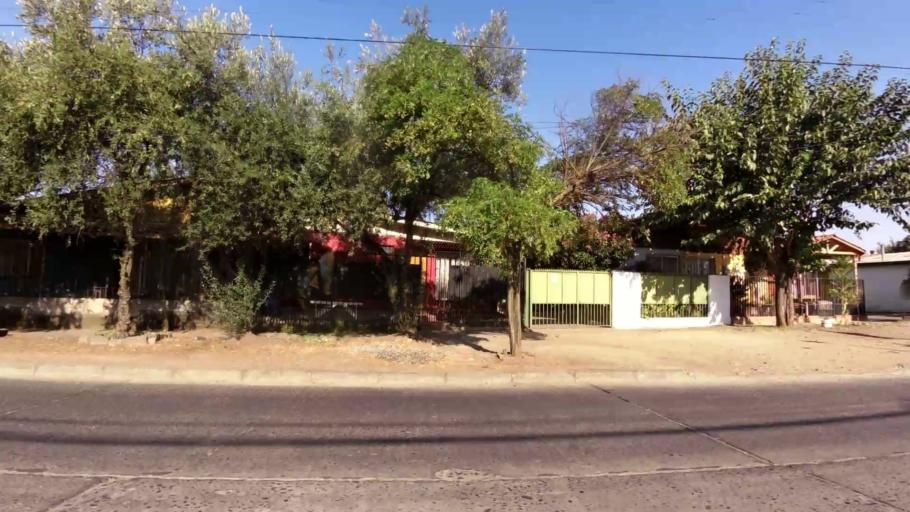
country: CL
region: Maule
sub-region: Provincia de Talca
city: Talca
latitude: -35.4373
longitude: -71.6703
